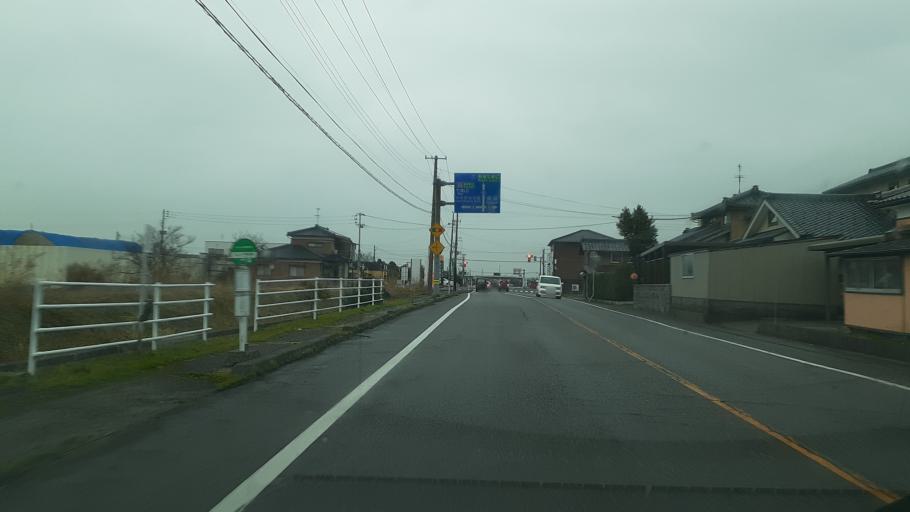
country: JP
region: Niigata
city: Kameda-honcho
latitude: 37.8800
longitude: 139.1261
